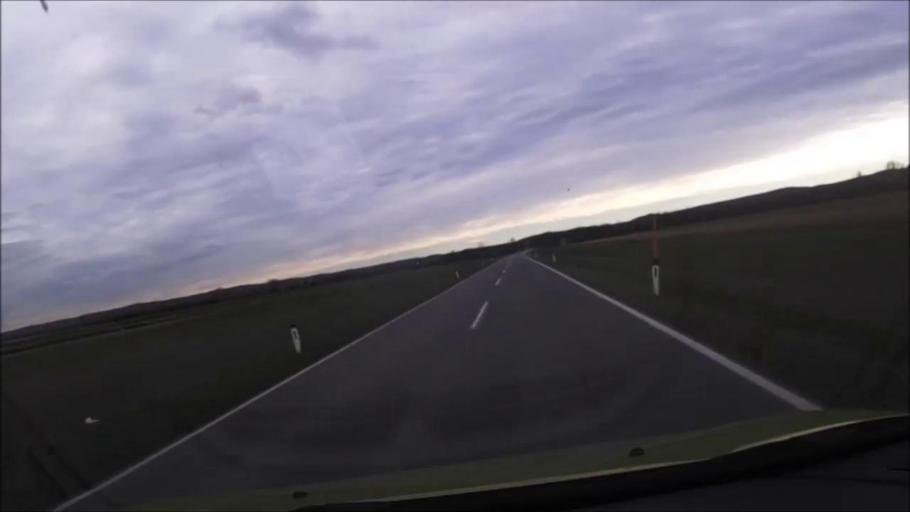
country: AT
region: Burgenland
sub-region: Eisenstadt-Umgebung
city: Leithaprodersdorf
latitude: 47.9485
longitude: 16.4554
